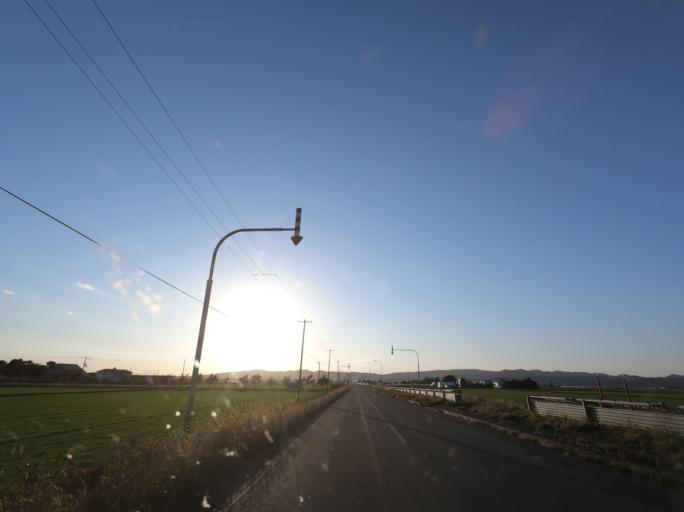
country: JP
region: Hokkaido
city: Iwamizawa
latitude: 42.9787
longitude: 141.8321
